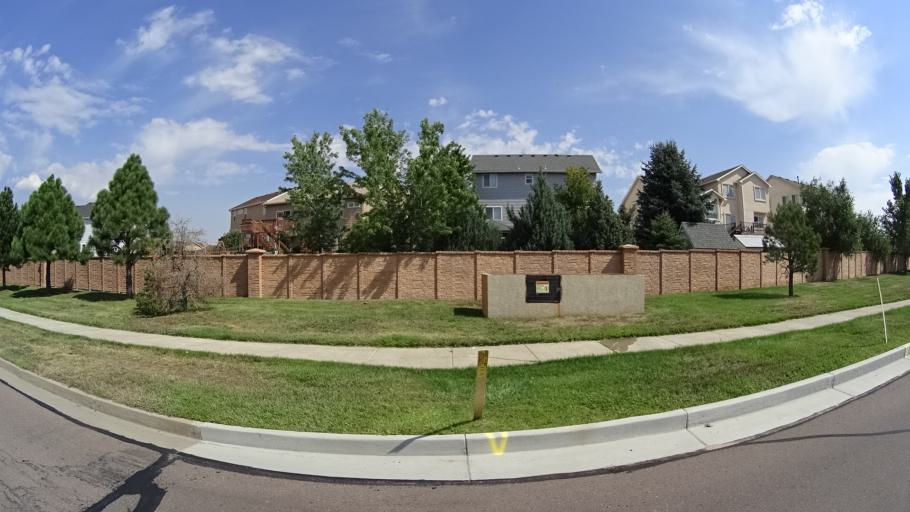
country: US
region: Colorado
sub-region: El Paso County
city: Cimarron Hills
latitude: 38.9295
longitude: -104.7264
